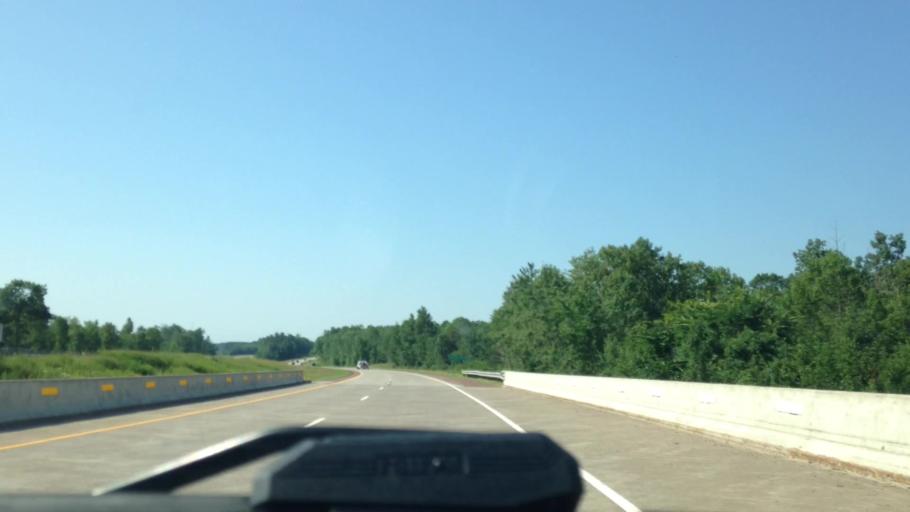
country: US
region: Wisconsin
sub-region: Douglas County
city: Lake Nebagamon
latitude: 46.3977
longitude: -91.8185
